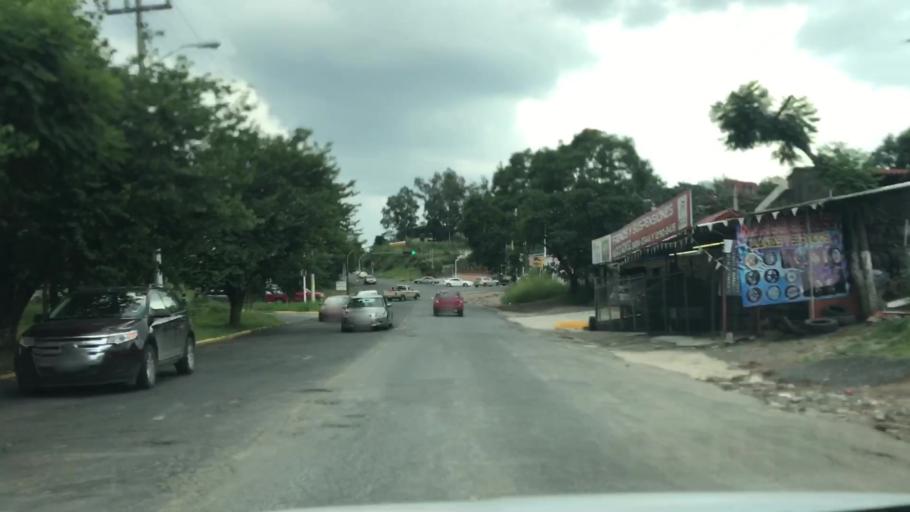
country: MX
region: Jalisco
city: Guadalajara
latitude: 20.6207
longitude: -103.4082
